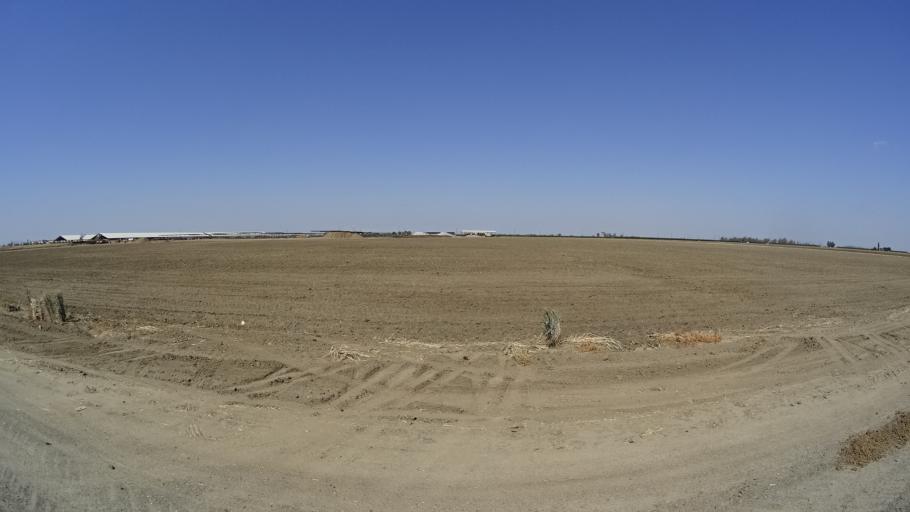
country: US
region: California
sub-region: Kings County
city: Home Garden
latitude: 36.2025
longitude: -119.6368
